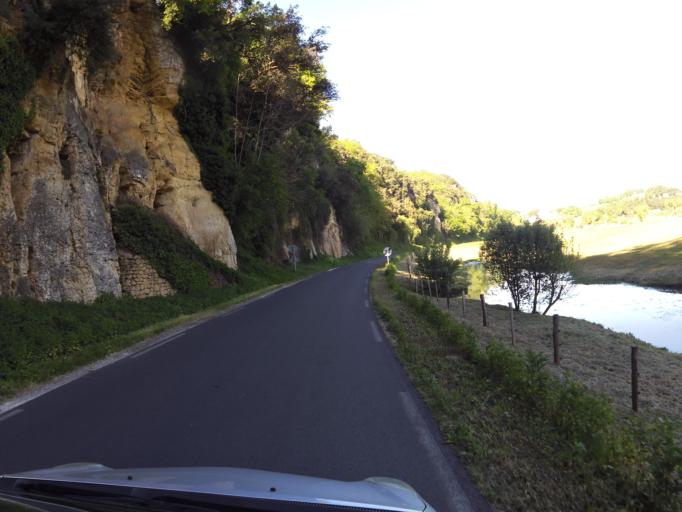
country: FR
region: Aquitaine
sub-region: Departement de la Dordogne
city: Carsac-Aillac
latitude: 44.8288
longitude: 1.2273
